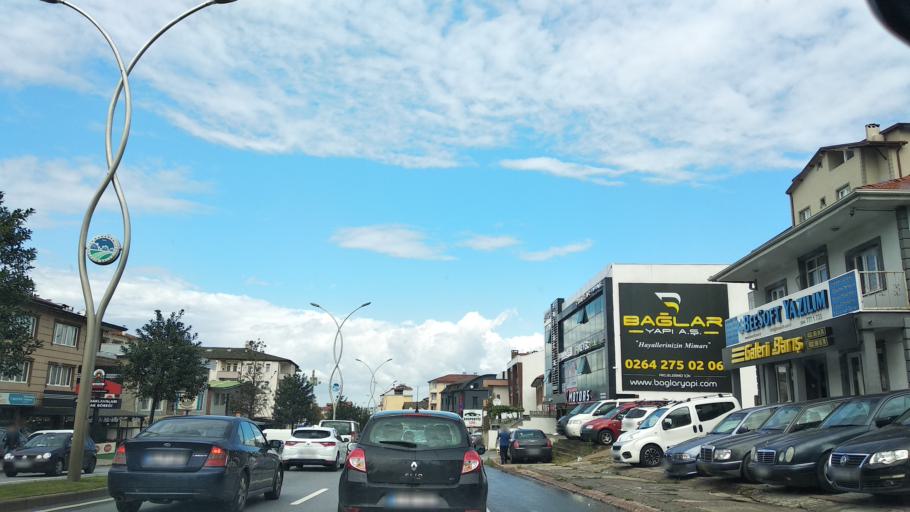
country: TR
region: Sakarya
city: Adapazari
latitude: 40.7495
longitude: 30.3857
